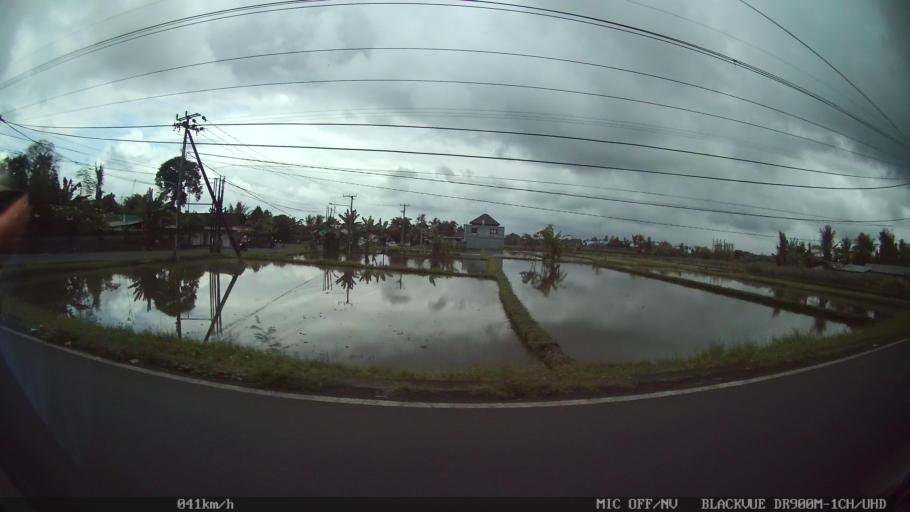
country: ID
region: Bali
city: Banjar Mambalkajanan
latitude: -8.5474
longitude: 115.2222
